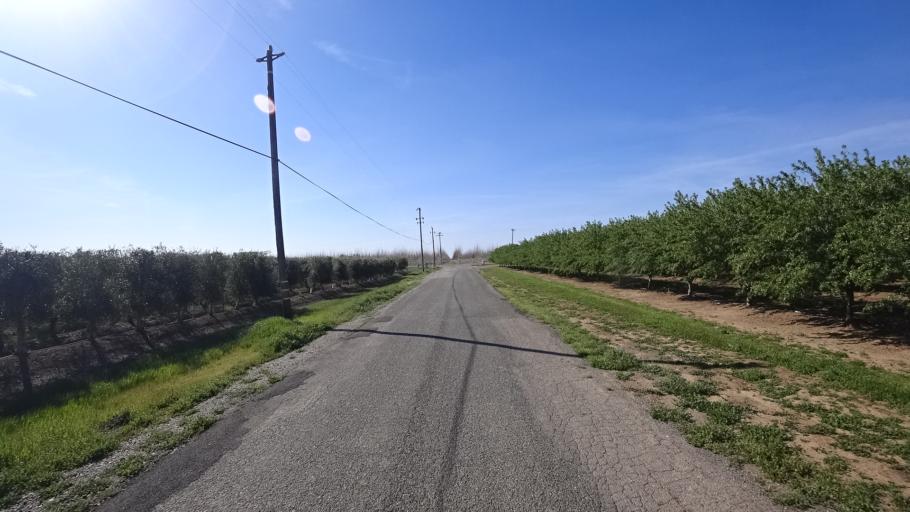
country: US
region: California
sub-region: Glenn County
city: Willows
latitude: 39.6254
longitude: -122.2160
